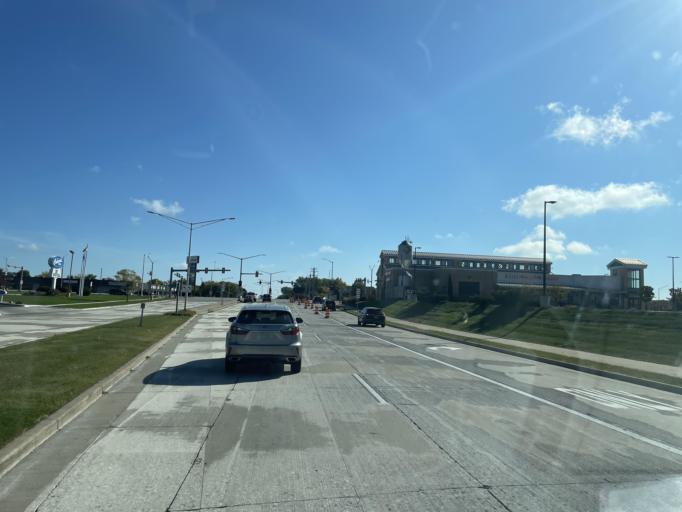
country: US
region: Wisconsin
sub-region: Milwaukee County
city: Oak Creek
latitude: 42.9011
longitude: -87.9134
